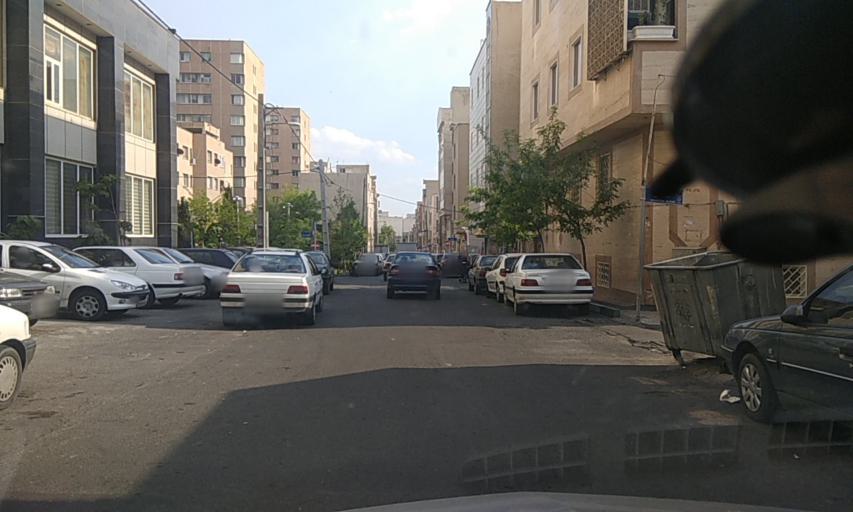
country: IR
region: Tehran
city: Tehran
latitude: 35.6870
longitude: 51.3787
